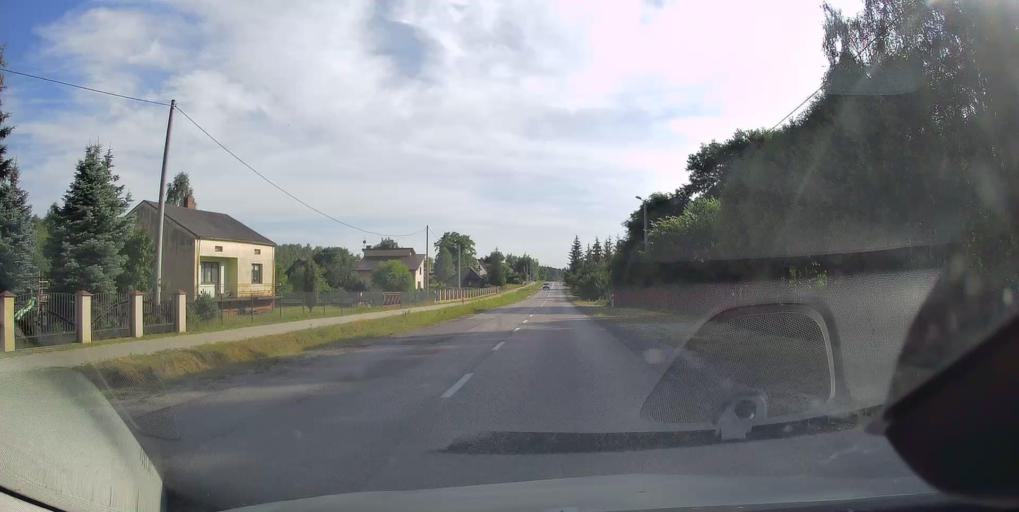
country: PL
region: Swietokrzyskie
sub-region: Powiat konecki
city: Radoszyce
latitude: 51.0855
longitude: 20.2879
